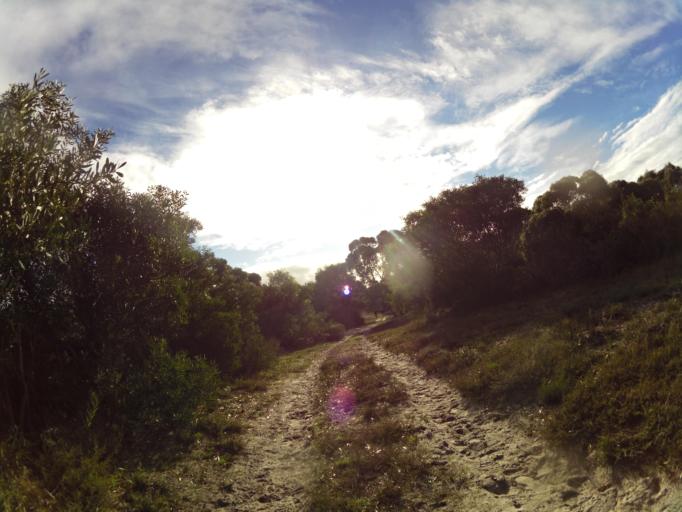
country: AU
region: Victoria
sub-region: Bass Coast
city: North Wonthaggi
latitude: -38.6294
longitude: 145.5717
